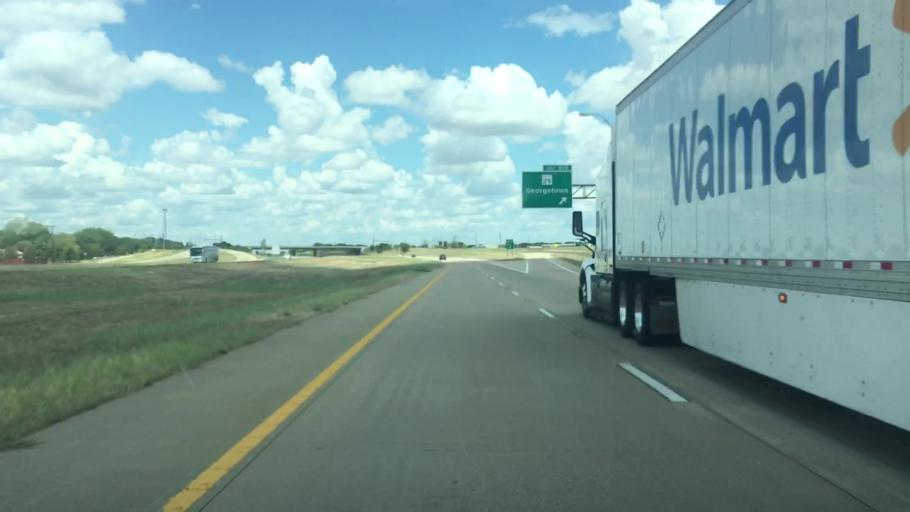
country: US
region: Texas
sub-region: Williamson County
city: Georgetown
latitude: 30.6353
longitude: -97.6281
